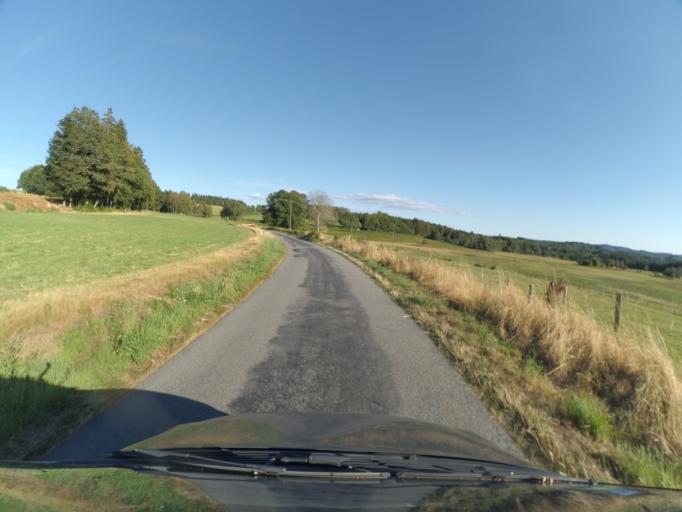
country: FR
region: Limousin
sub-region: Departement de la Creuse
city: Banize
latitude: 45.7341
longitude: 2.0403
